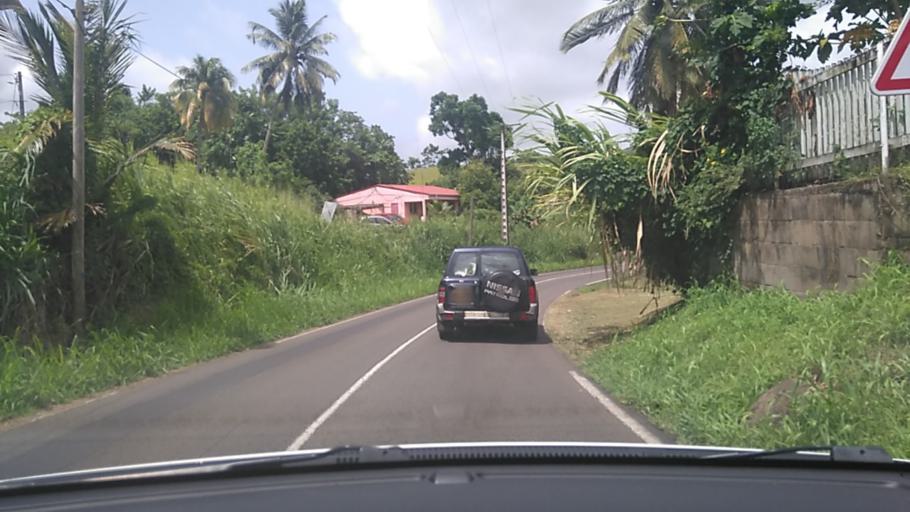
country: MQ
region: Martinique
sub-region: Martinique
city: Saint-Esprit
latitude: 14.5595
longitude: -60.9265
